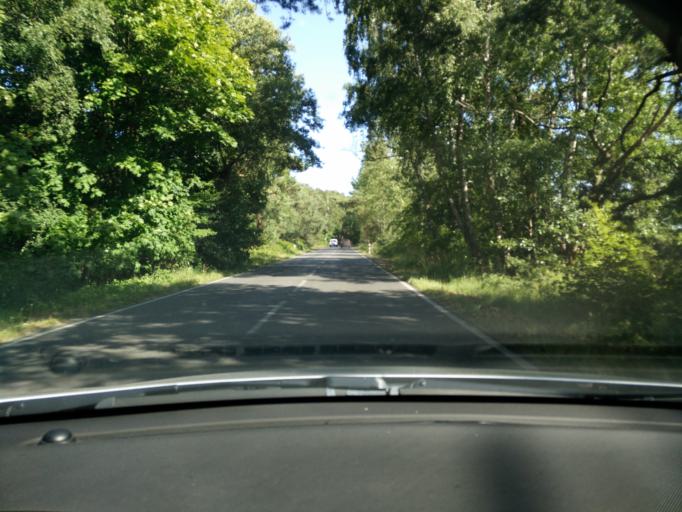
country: PL
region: Pomeranian Voivodeship
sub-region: Powiat pucki
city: Jastarnia
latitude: 54.7186
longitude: 18.6274
